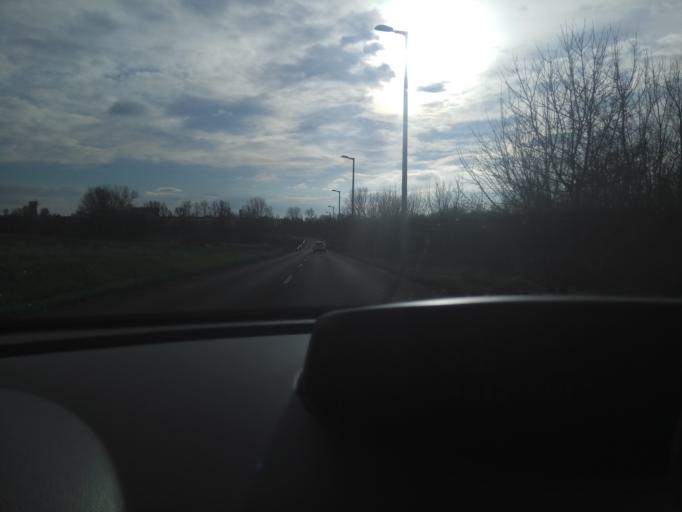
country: HU
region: Budapest
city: Budapest XV. keruelet
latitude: 47.5947
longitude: 19.1230
